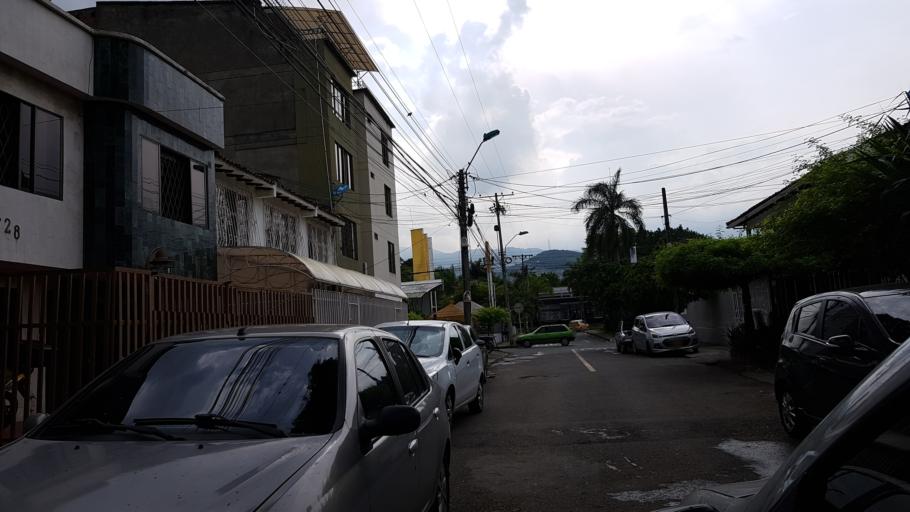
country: CO
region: Valle del Cauca
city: Cali
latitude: 3.3879
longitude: -76.5438
